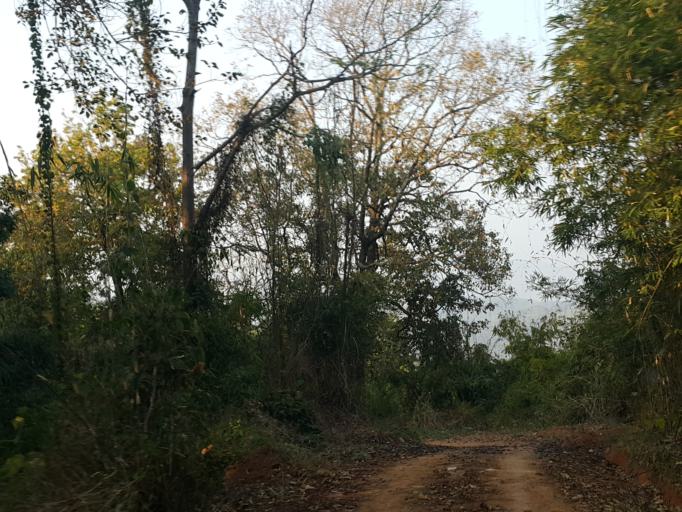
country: TH
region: Chiang Mai
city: Mae Taeng
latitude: 19.0465
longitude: 98.7672
